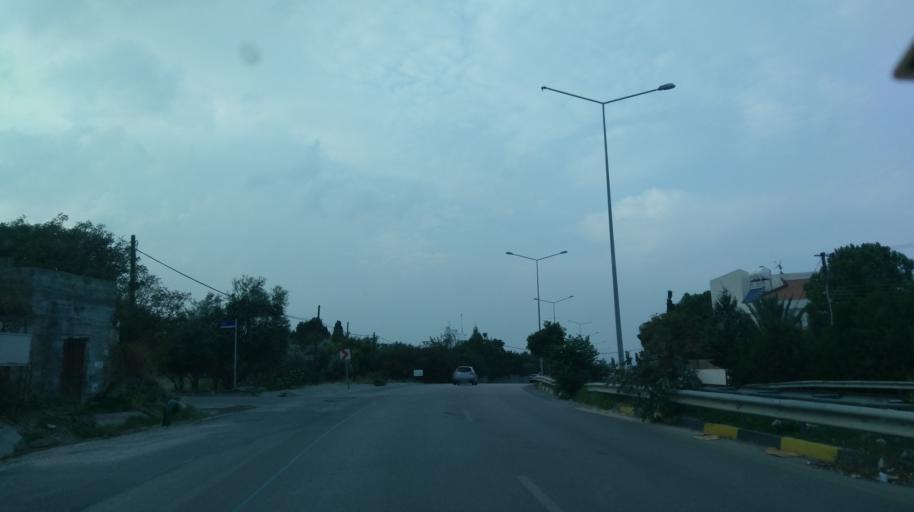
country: CY
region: Keryneia
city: Kyrenia
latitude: 35.3364
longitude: 33.2582
